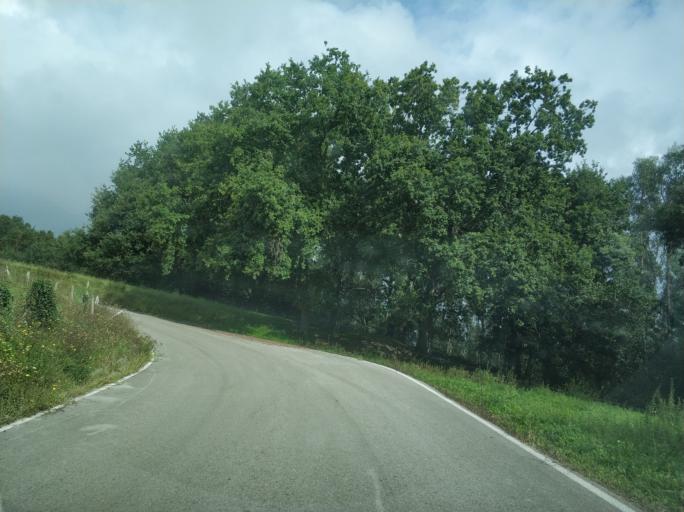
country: ES
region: Cantabria
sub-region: Provincia de Cantabria
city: San Miguel de Meruelo
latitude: 43.4337
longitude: -3.5771
